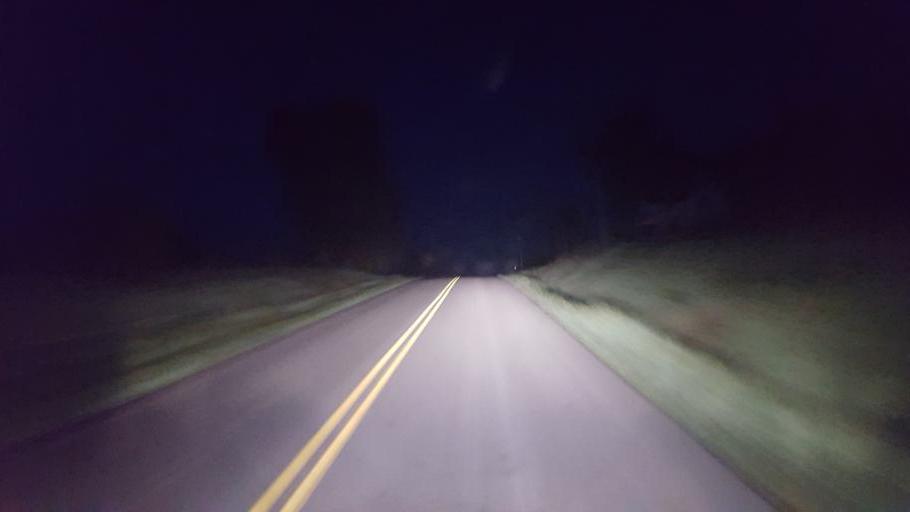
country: US
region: Iowa
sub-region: Decatur County
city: Lamoni
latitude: 40.4516
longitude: -93.8220
